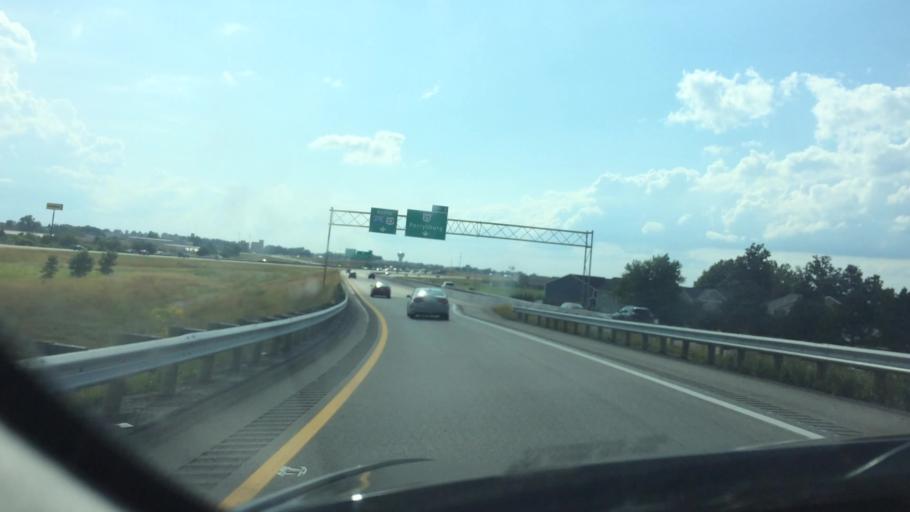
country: US
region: Ohio
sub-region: Wood County
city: Perrysburg
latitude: 41.5332
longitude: -83.6244
